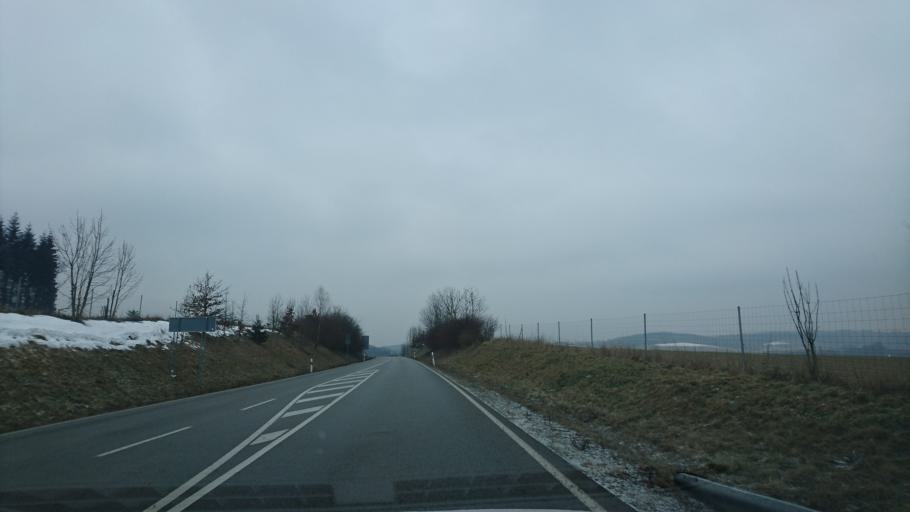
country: DE
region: Bavaria
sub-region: Lower Bavaria
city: Bad Griesbach
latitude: 48.4492
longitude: 13.1768
